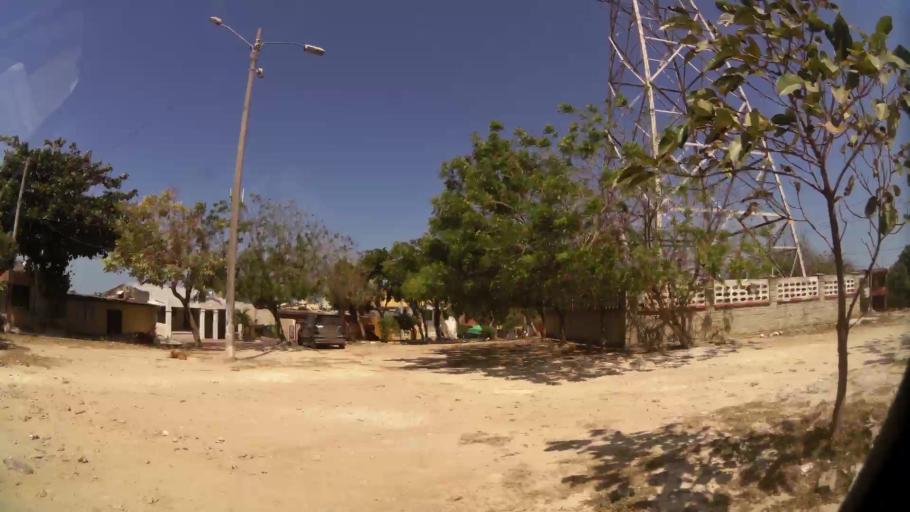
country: CO
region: Atlantico
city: Barranquilla
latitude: 10.9818
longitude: -74.8186
